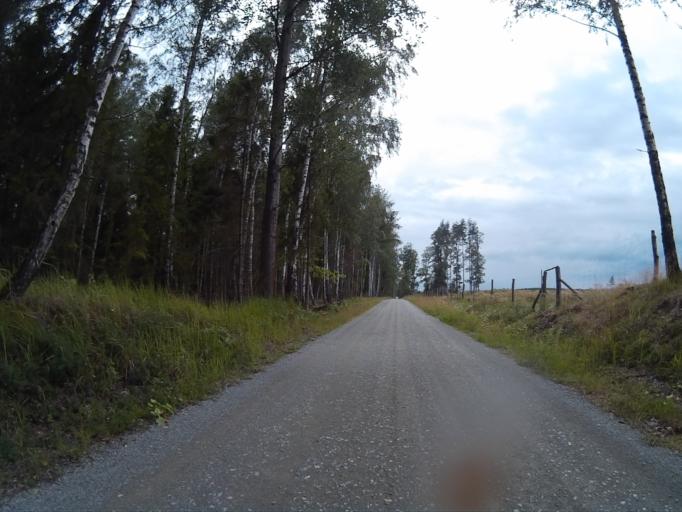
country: PL
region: Kujawsko-Pomorskie
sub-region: Powiat swiecki
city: Lniano
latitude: 53.6188
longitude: 18.2186
